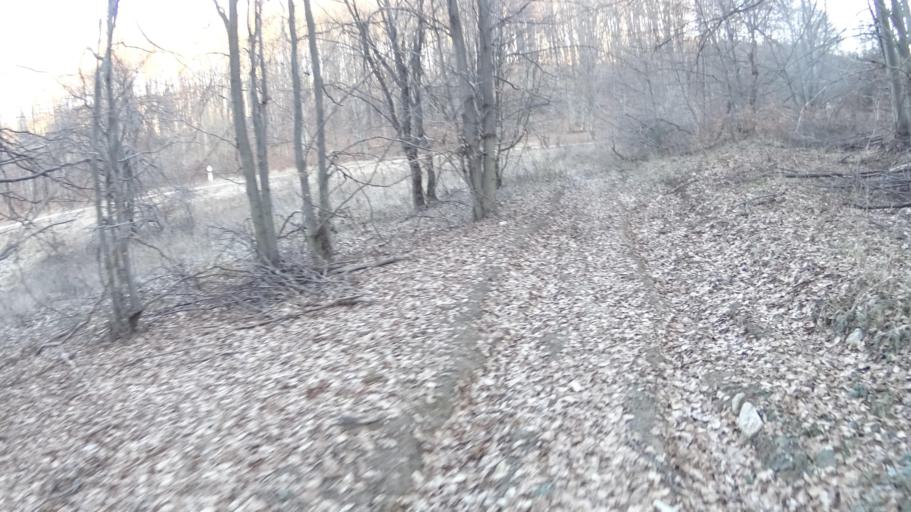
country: HU
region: Heves
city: Szilvasvarad
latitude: 48.0930
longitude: 20.4829
